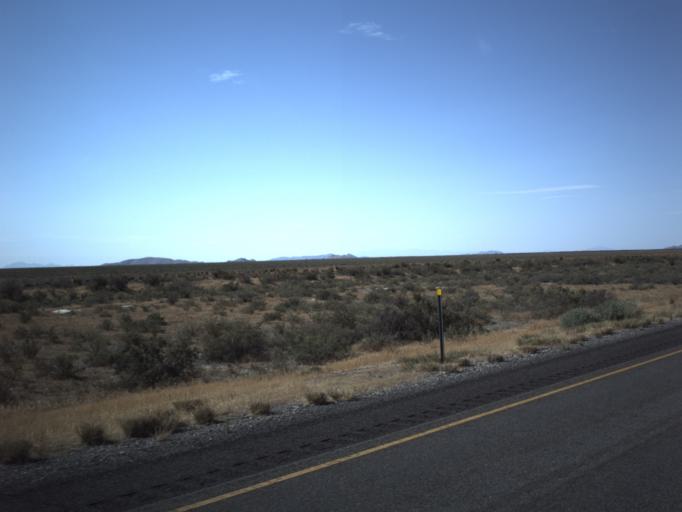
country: US
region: Utah
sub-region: Tooele County
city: Grantsville
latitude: 40.7422
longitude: -113.0785
